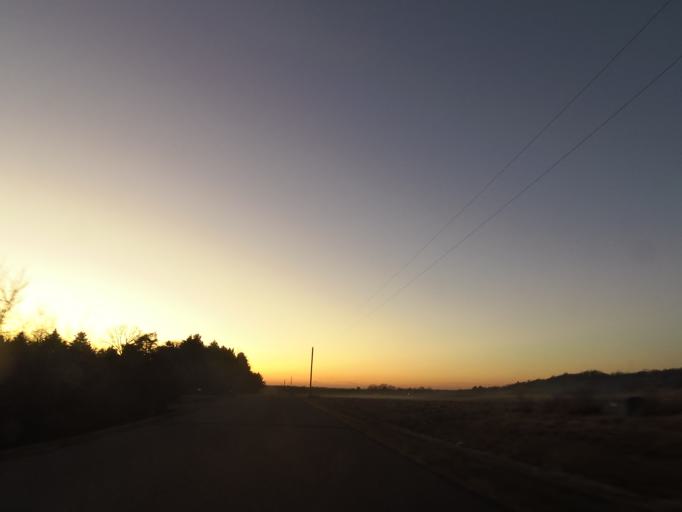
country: US
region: Wisconsin
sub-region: Pierce County
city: River Falls
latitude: 44.9313
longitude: -92.6749
